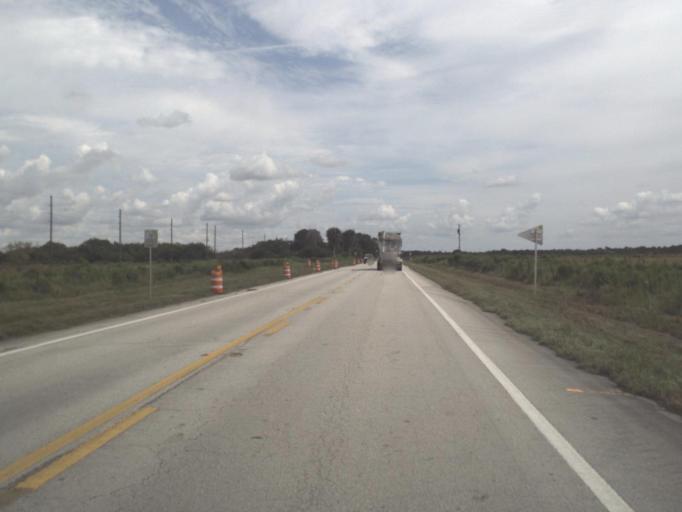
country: US
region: Florida
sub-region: Okeechobee County
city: Taylor Creek
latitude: 27.2643
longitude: -80.7402
